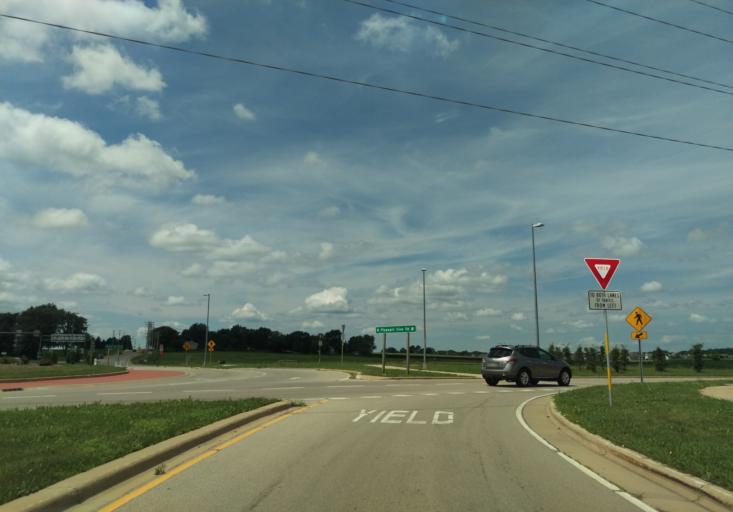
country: US
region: Wisconsin
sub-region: Dane County
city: Middleton
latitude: 43.0605
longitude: -89.5367
